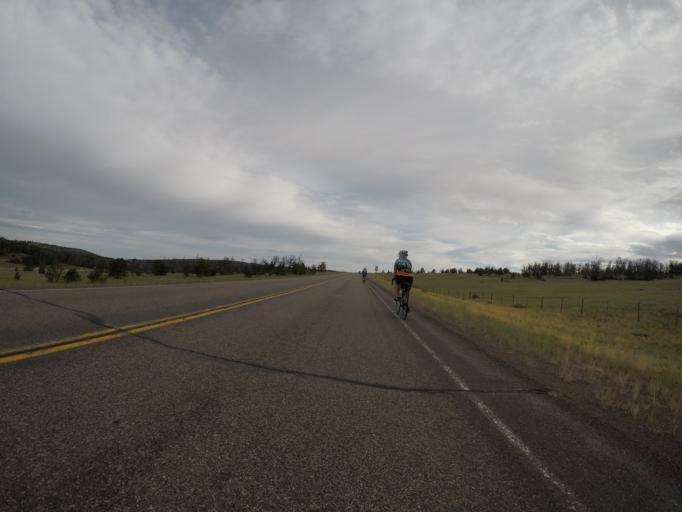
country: US
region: Wyoming
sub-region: Albany County
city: Laramie
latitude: 41.2422
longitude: -105.4363
